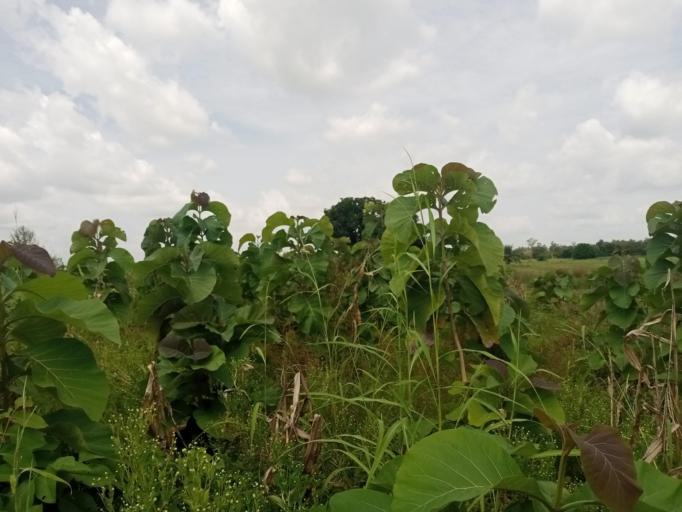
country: TG
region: Plateaux
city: Notse
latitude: 6.7773
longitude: 1.1198
